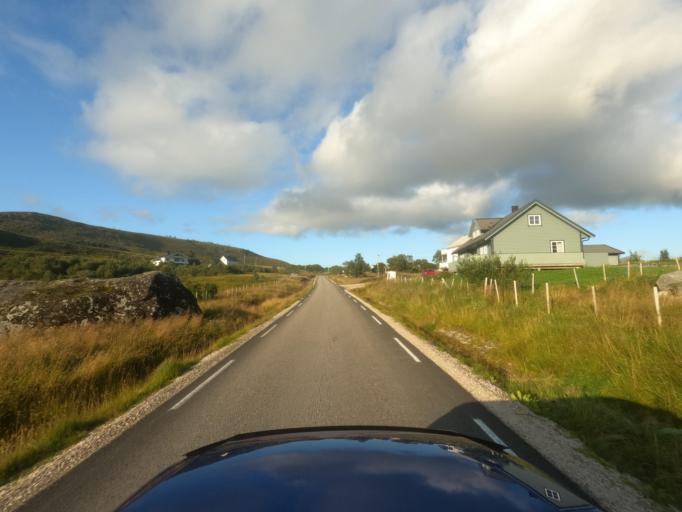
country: NO
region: Nordland
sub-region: Vestvagoy
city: Gravdal
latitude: 68.1200
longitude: 13.4957
